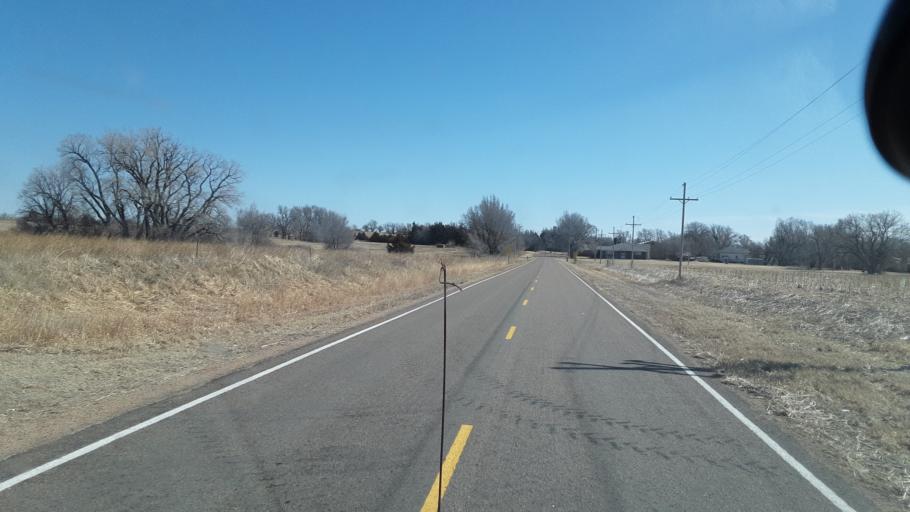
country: US
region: Kansas
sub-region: Barton County
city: Ellinwood
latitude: 38.2820
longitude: -98.4206
